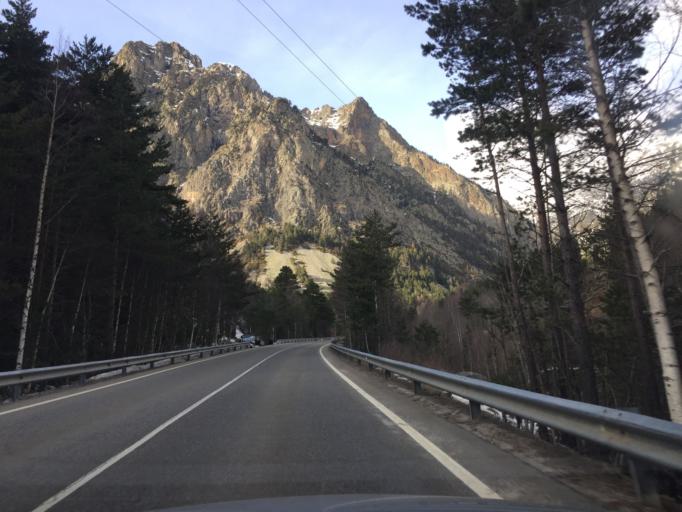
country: ES
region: Aragon
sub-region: Provincia de Huesca
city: Bielsa
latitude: 42.6998
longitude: 0.2021
